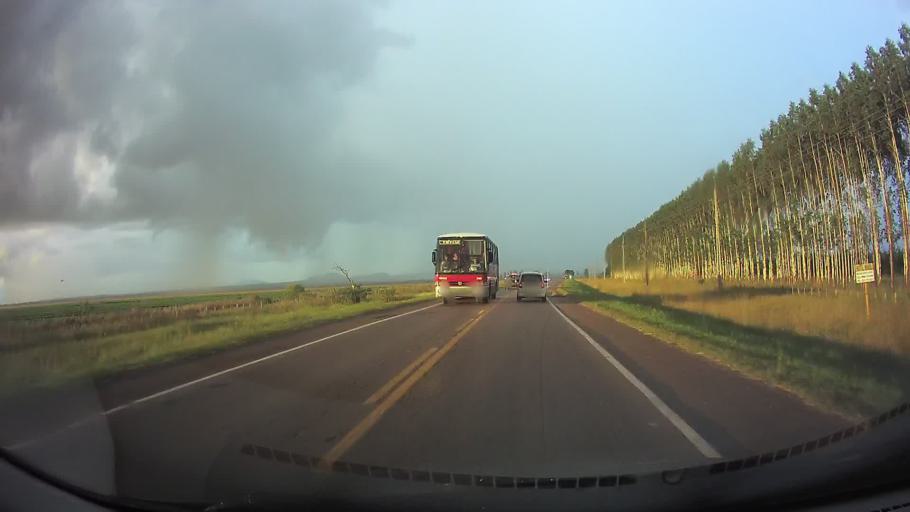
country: PY
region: Paraguari
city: Paraguari
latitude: -25.6742
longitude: -57.1662
